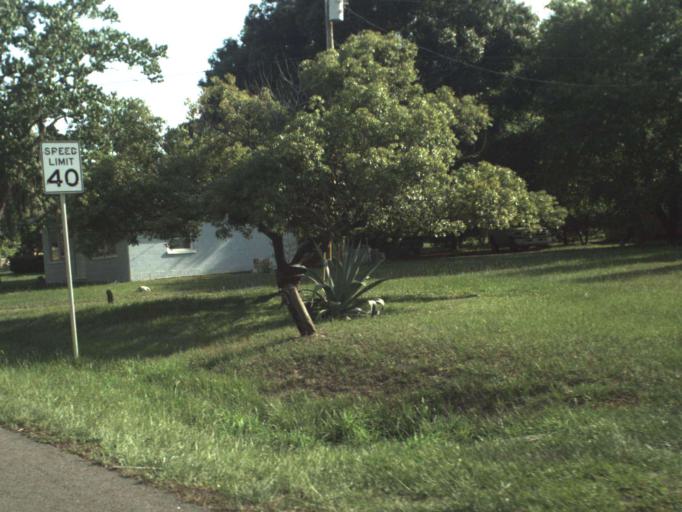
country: US
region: Florida
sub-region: Lake County
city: Groveland
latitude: 28.5525
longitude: -81.8516
